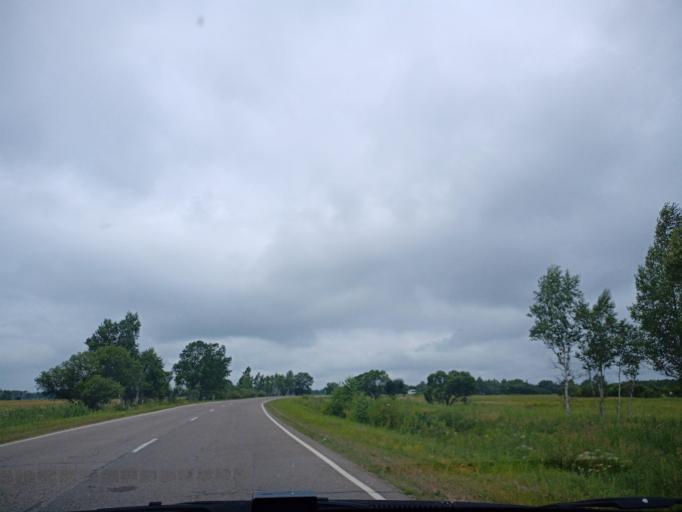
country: RU
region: Primorskiy
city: Novopokrovka
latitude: 45.9642
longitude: 134.2559
